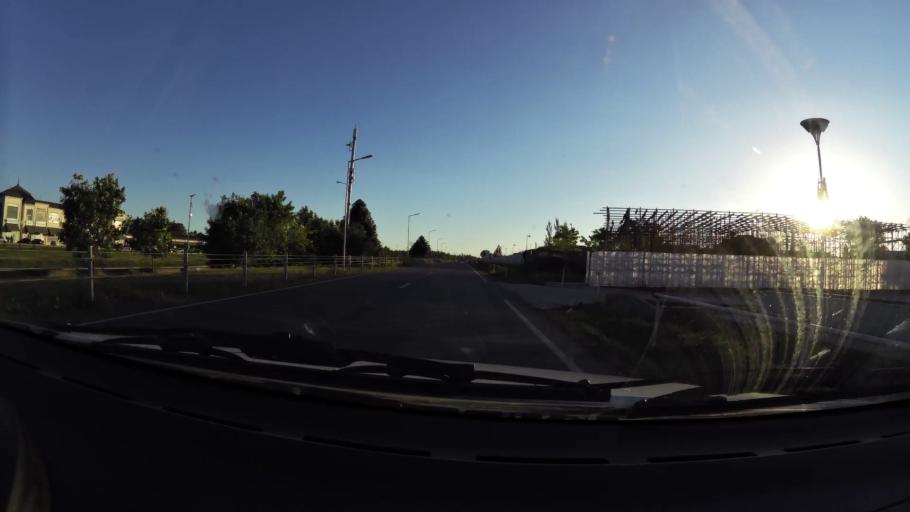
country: AR
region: Buenos Aires
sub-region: Partido de Quilmes
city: Quilmes
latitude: -34.7954
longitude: -58.1606
